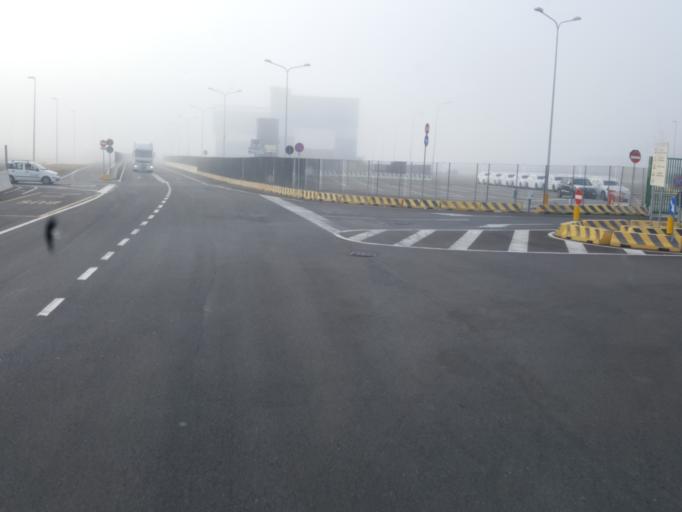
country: IT
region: Latium
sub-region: Citta metropolitana di Roma Capitale
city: Civitavecchia
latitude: 42.1098
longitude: 11.7732
